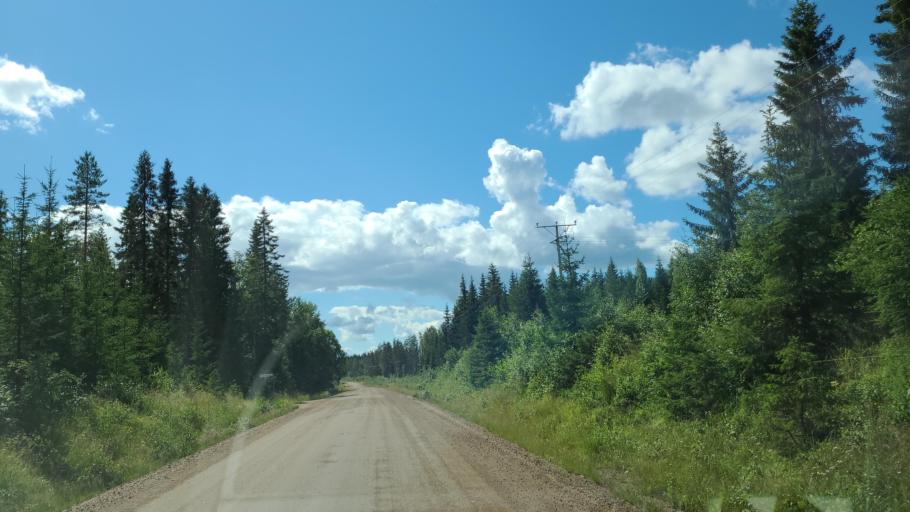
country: FI
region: Northern Savo
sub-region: Koillis-Savo
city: Kaavi
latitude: 62.9455
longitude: 28.7643
